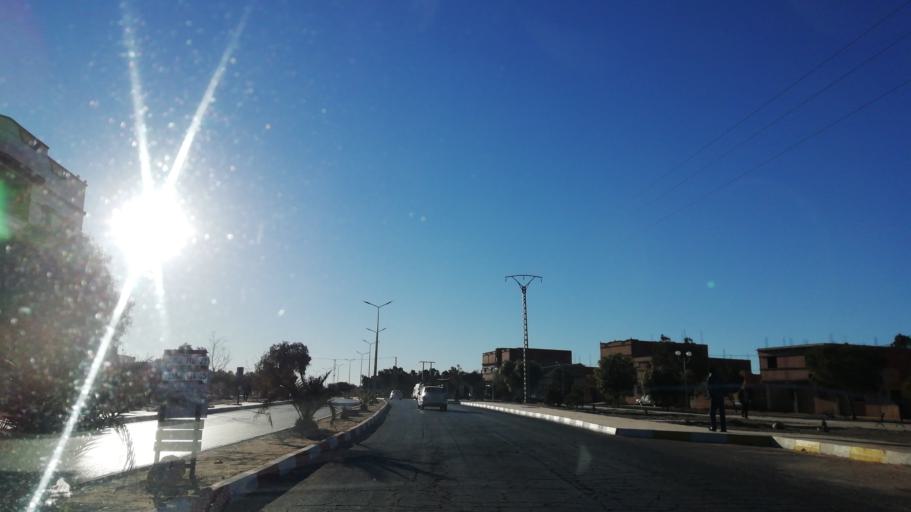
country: DZ
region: Saida
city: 'Ain el Hadjar
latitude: 34.0330
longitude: 0.0883
